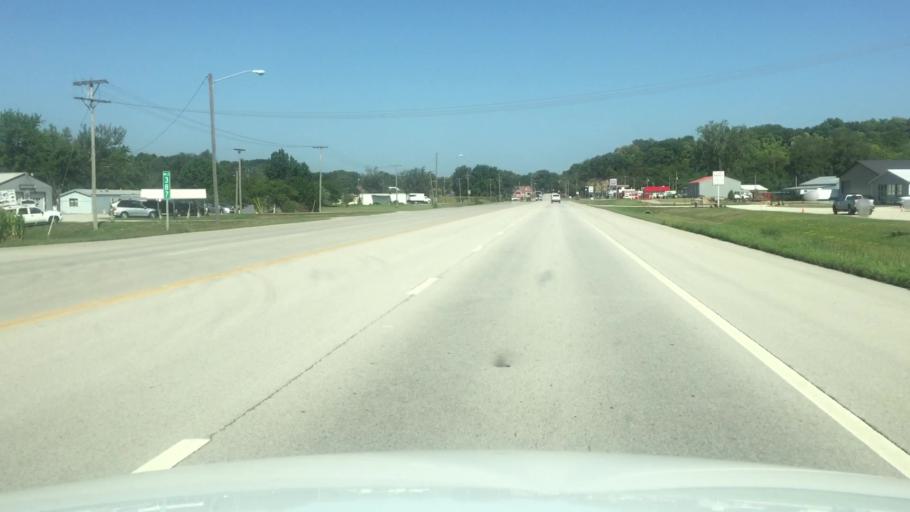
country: US
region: Kansas
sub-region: Doniphan County
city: Wathena
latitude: 39.7566
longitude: -94.9397
